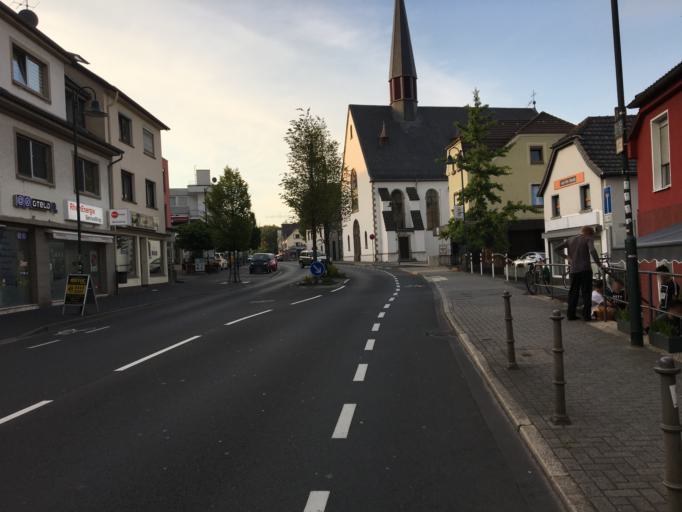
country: DE
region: North Rhine-Westphalia
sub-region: Regierungsbezirk Koln
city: Rosrath
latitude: 50.8968
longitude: 7.1829
